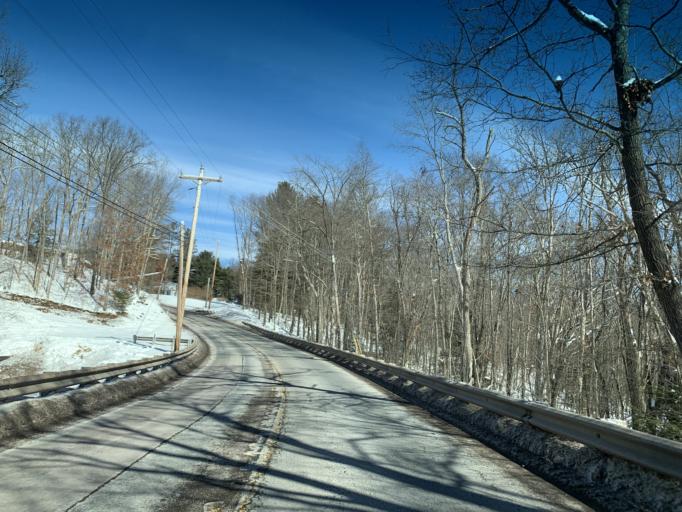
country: US
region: West Virginia
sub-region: Preston County
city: Terra Alta
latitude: 39.6881
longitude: -79.4407
